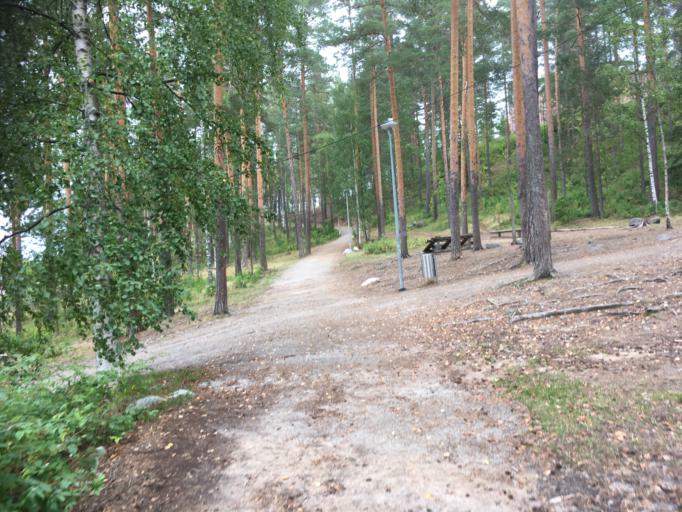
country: FI
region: Central Finland
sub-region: Jyvaeskylae
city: Jyvaeskylae
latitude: 62.2425
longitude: 25.7370
